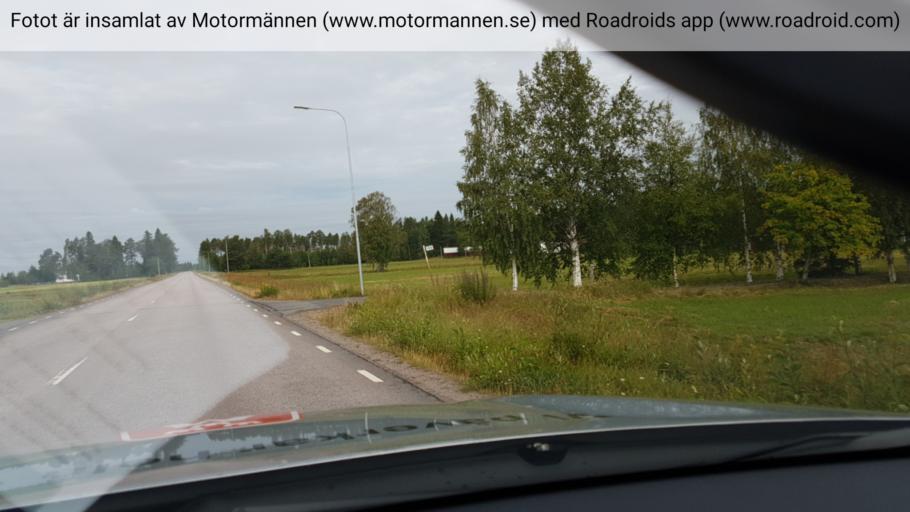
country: SE
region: Norrbotten
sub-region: Lulea Kommun
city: Sodra Sunderbyn
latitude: 65.6396
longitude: 21.9041
